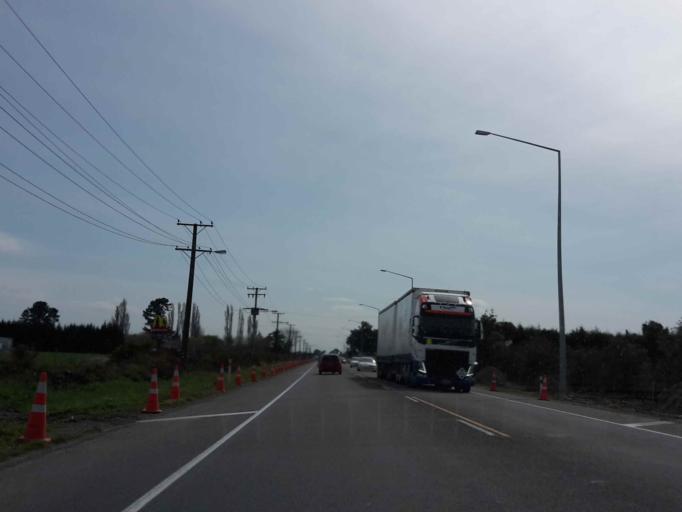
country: NZ
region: Canterbury
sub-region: Christchurch City
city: Christchurch
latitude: -43.4843
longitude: 172.5543
